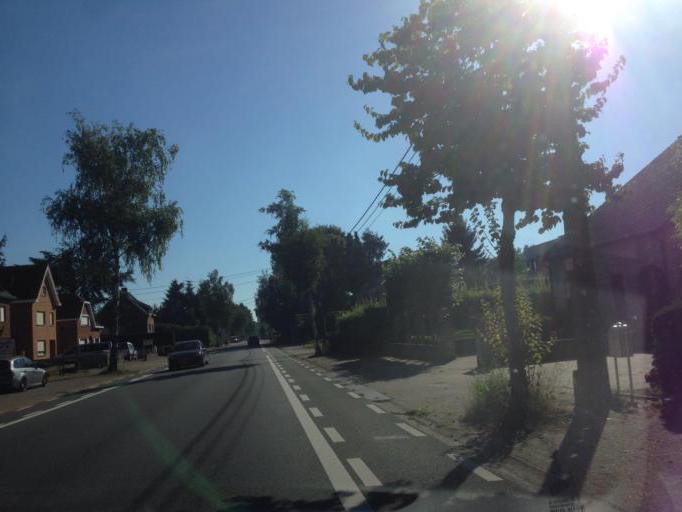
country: BE
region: Flanders
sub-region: Provincie Antwerpen
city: Geel
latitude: 51.1640
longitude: 5.0232
